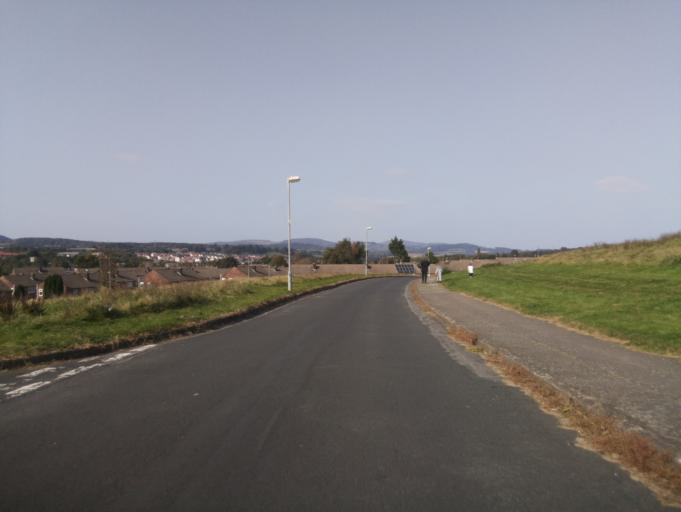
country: GB
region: Wales
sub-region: Newport
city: Marshfield
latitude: 51.5252
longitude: -3.1203
